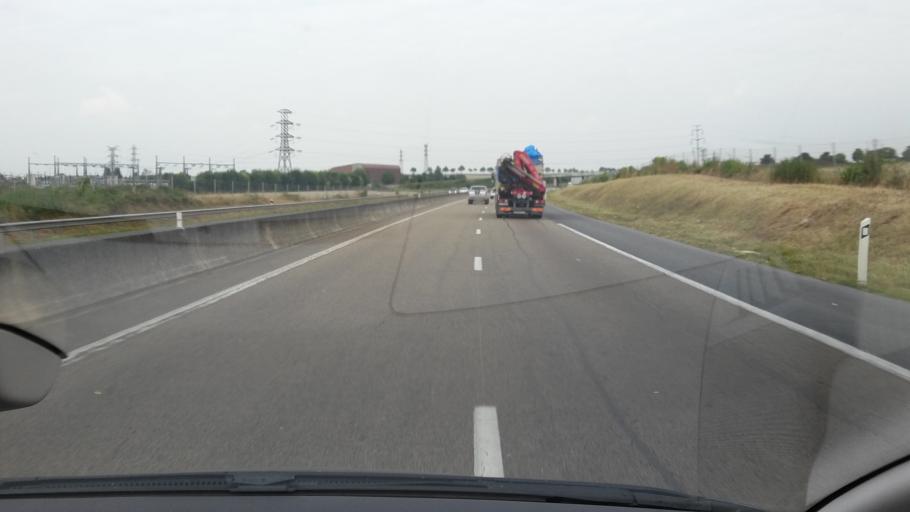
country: FR
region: Champagne-Ardenne
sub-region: Departement de la Marne
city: Cernay-les-Reims
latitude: 49.2680
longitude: 4.0869
